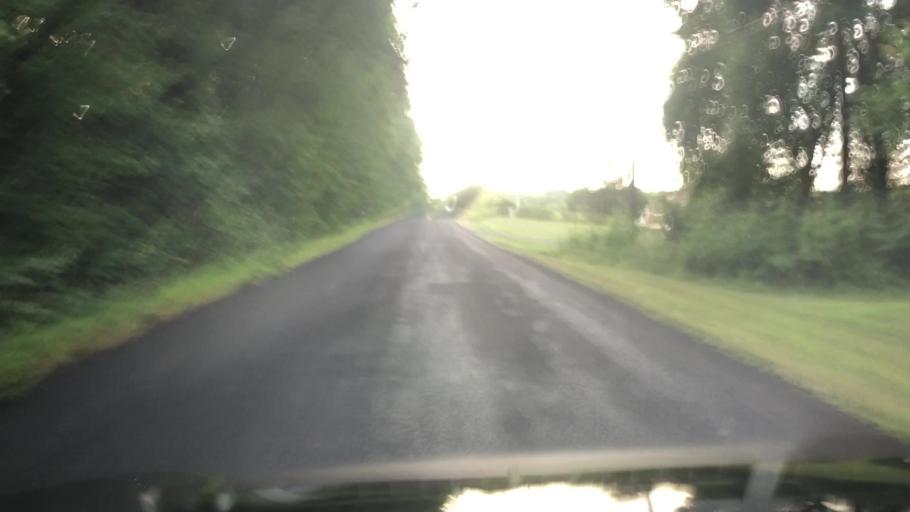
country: US
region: Virginia
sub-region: Fauquier County
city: New Baltimore
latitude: 38.7152
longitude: -77.6746
